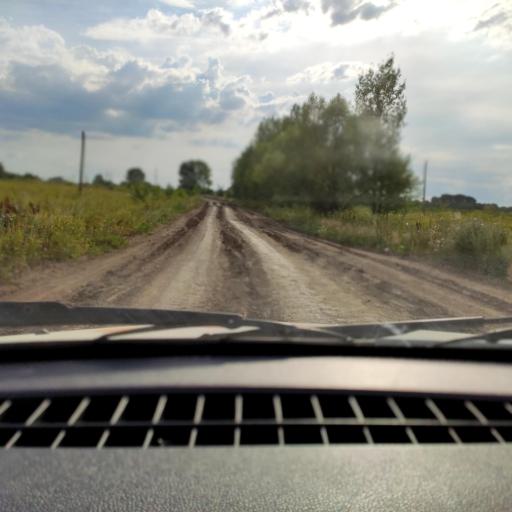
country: RU
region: Bashkortostan
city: Blagoveshchensk
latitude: 54.9292
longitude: 55.9542
